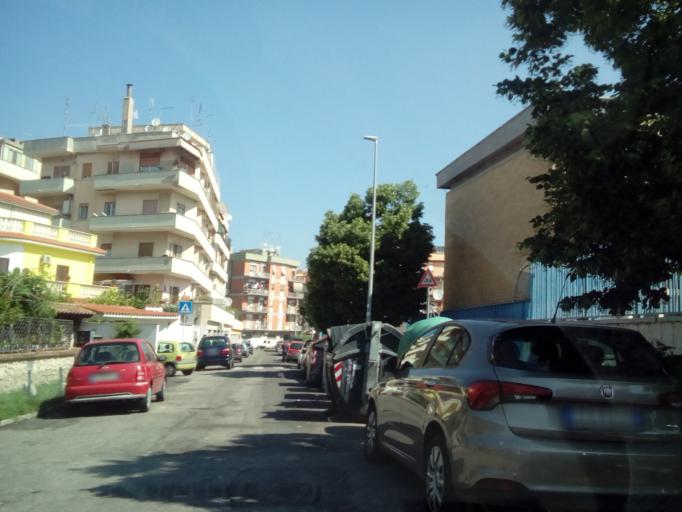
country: IT
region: Latium
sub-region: Citta metropolitana di Roma Capitale
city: Rome
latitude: 41.8756
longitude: 12.5732
